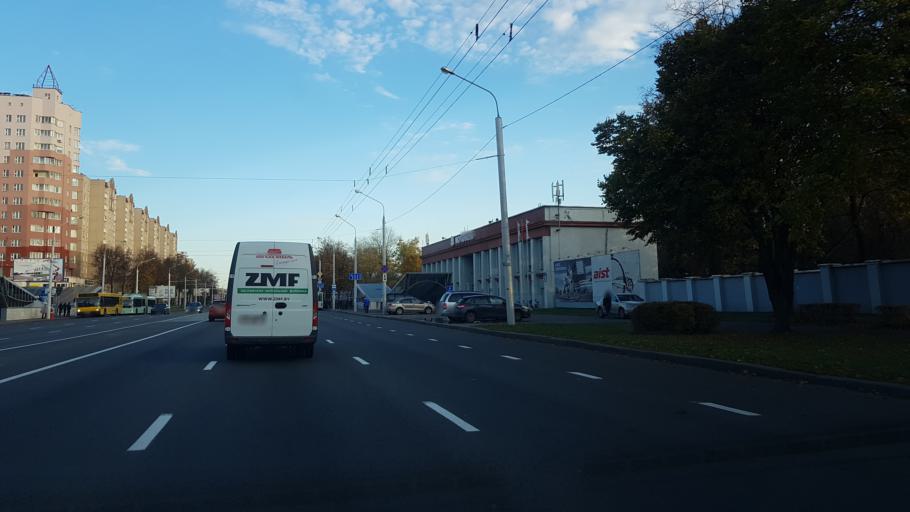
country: BY
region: Minsk
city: Minsk
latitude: 53.8839
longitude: 27.5908
